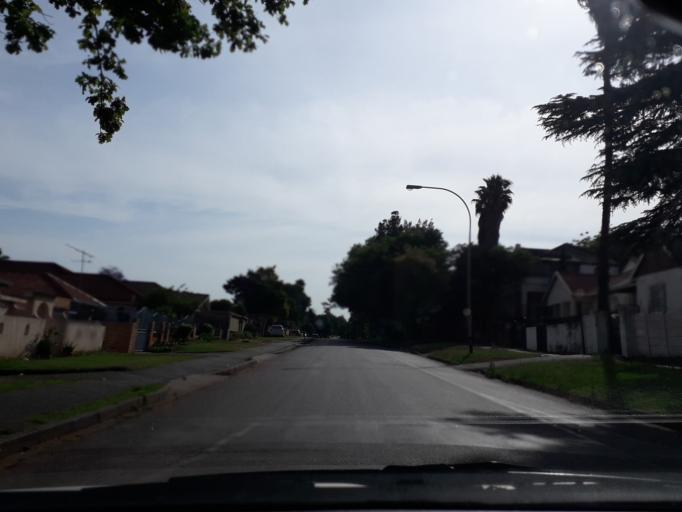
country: ZA
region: Gauteng
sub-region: City of Johannesburg Metropolitan Municipality
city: Johannesburg
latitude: -26.1865
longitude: 28.0792
